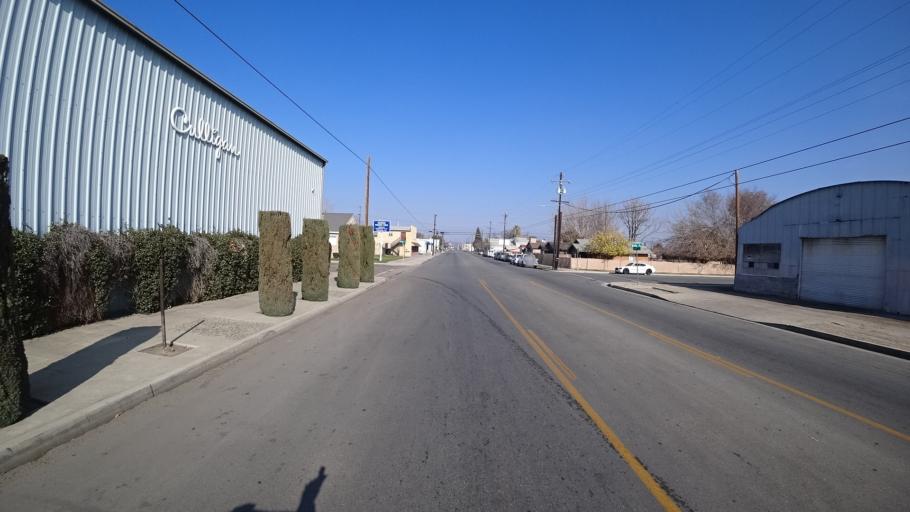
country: US
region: California
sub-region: Kern County
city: Bakersfield
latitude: 35.3693
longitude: -118.9957
